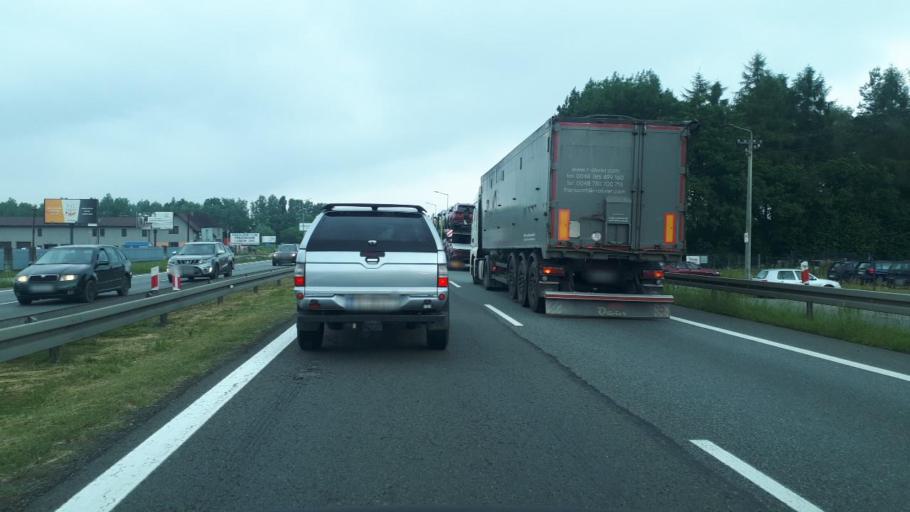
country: PL
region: Silesian Voivodeship
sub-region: Powiat pszczynski
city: Pszczyna
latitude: 49.9626
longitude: 18.9605
